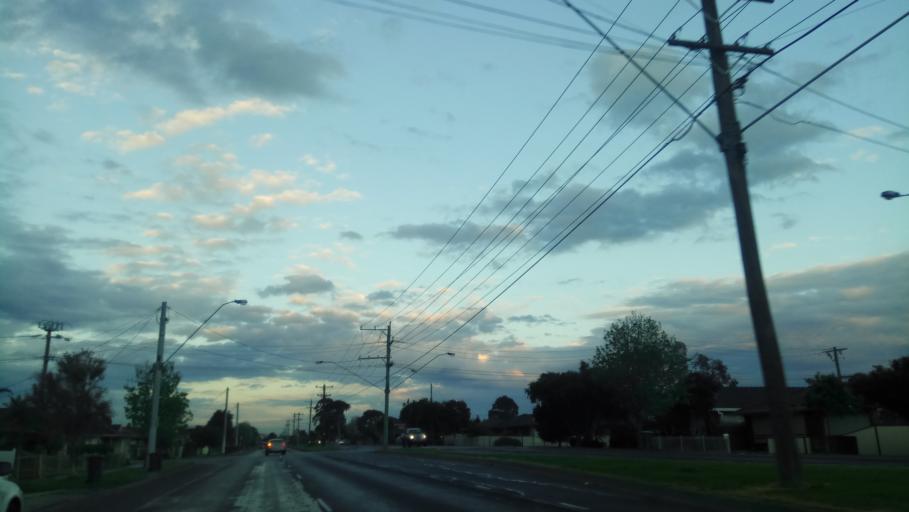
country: AU
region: Victoria
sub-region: Hobsons Bay
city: Laverton
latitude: -37.8713
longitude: 144.7739
